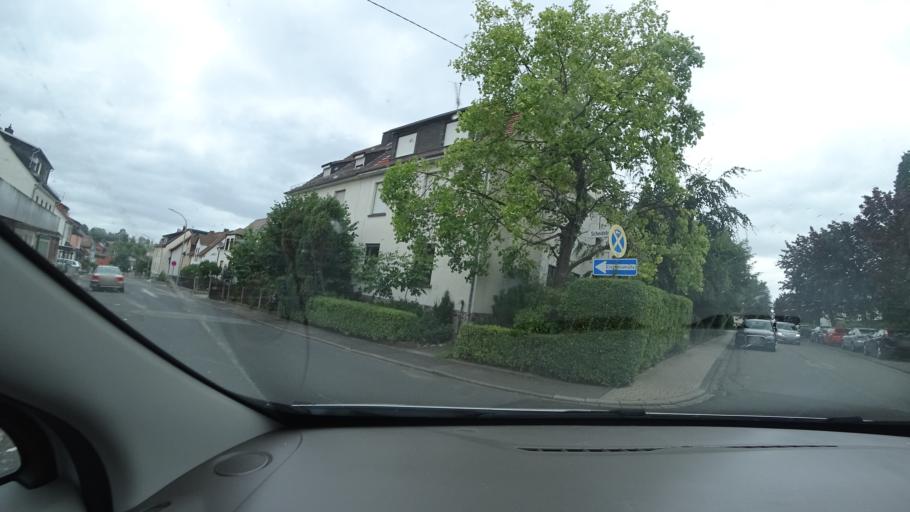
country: DE
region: Rheinland-Pfalz
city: Hohr-Grenzhausen
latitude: 50.4406
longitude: 7.6618
